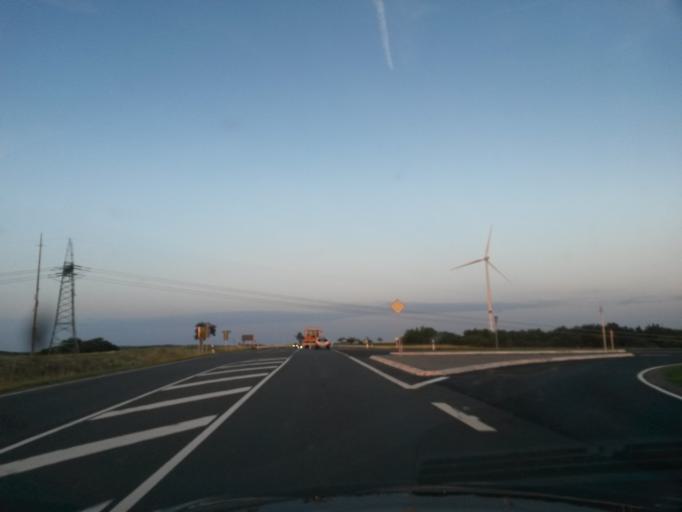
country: DE
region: Bavaria
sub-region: Regierungsbezirk Unterfranken
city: Holzkirchen
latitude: 49.8052
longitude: 9.6515
